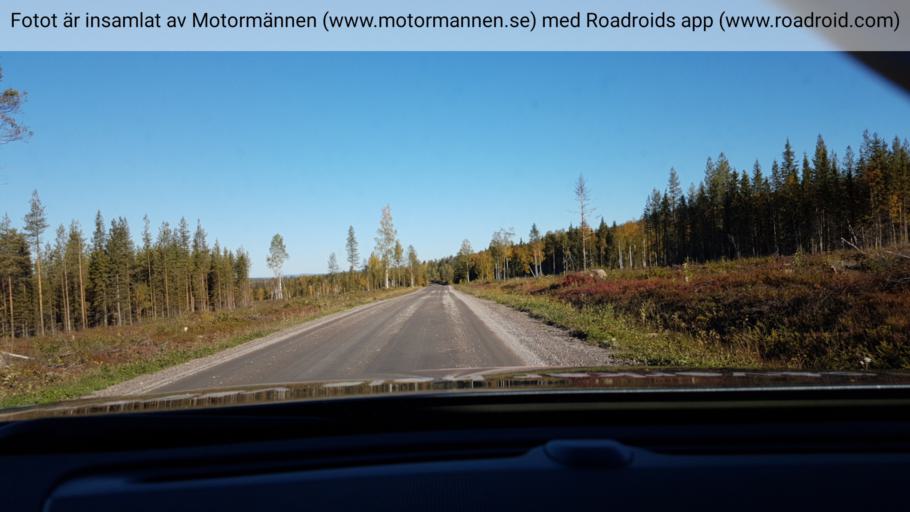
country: SE
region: Norrbotten
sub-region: Alvsbyns Kommun
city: AElvsbyn
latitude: 66.2067
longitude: 21.1737
